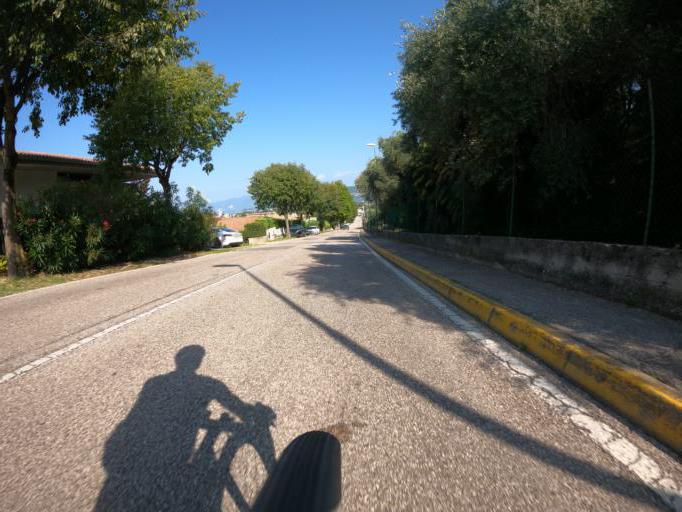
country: IT
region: Veneto
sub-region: Provincia di Verona
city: Bardolino
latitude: 45.5438
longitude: 10.7306
